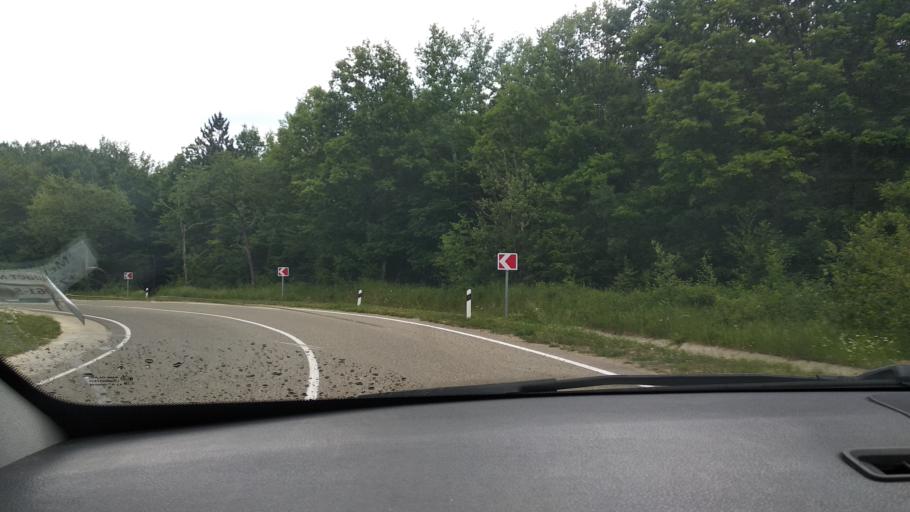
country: RU
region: Adygeya
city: Kamennomostskiy
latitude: 44.2699
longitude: 39.9470
